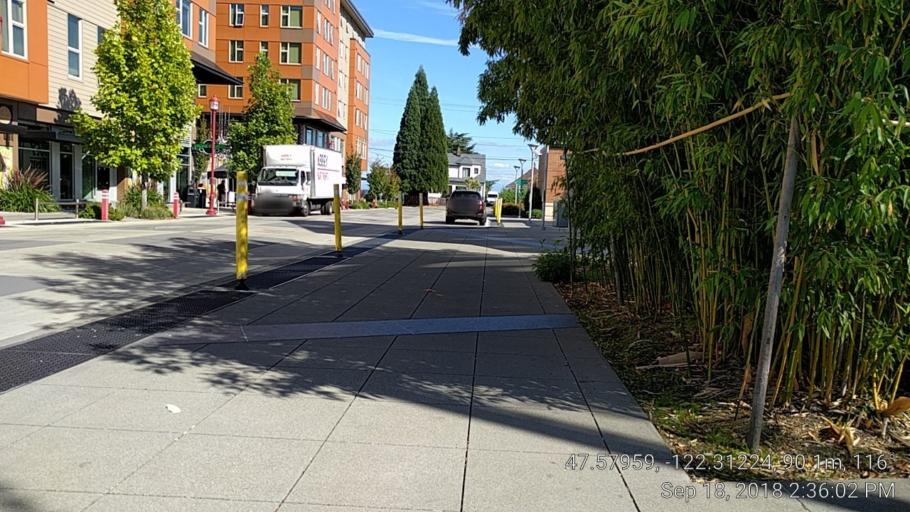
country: US
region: Washington
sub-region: King County
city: Seattle
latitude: 47.5796
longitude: -122.3122
